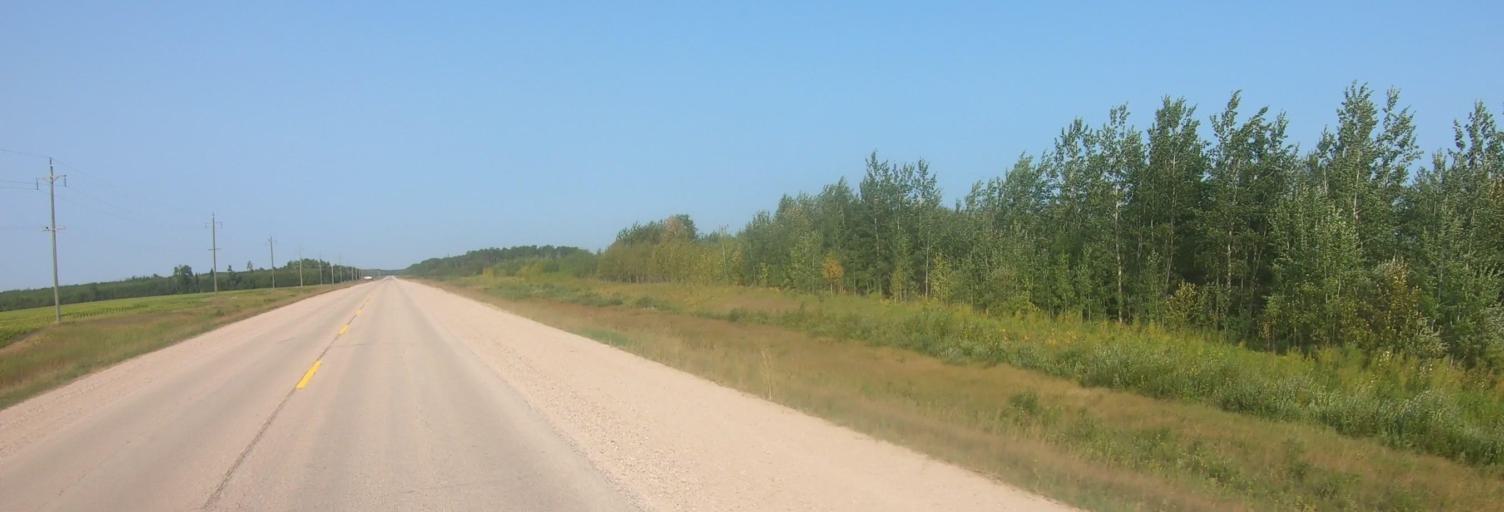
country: US
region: Minnesota
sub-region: Roseau County
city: Roseau
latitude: 49.0234
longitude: -95.7038
